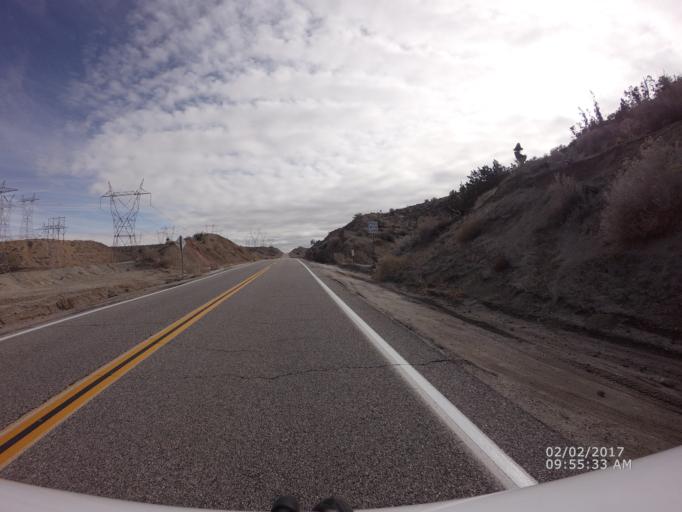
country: US
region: California
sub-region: Los Angeles County
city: Littlerock
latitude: 34.5062
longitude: -118.0250
